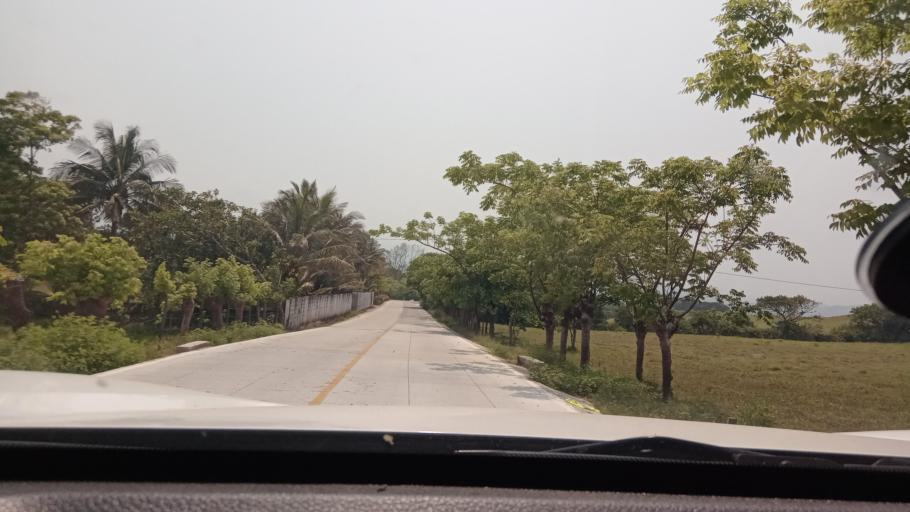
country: MX
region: Veracruz
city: Catemaco
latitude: 18.5578
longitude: -95.0106
